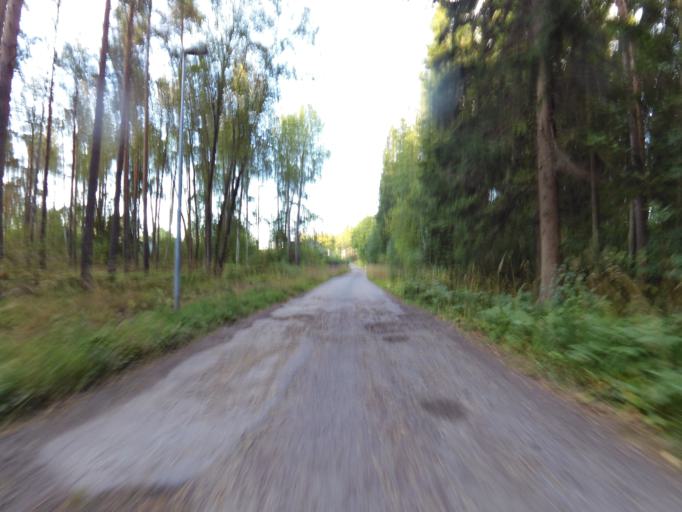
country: SE
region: Gaevleborg
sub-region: Gavle Kommun
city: Gavle
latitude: 60.6710
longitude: 17.2387
